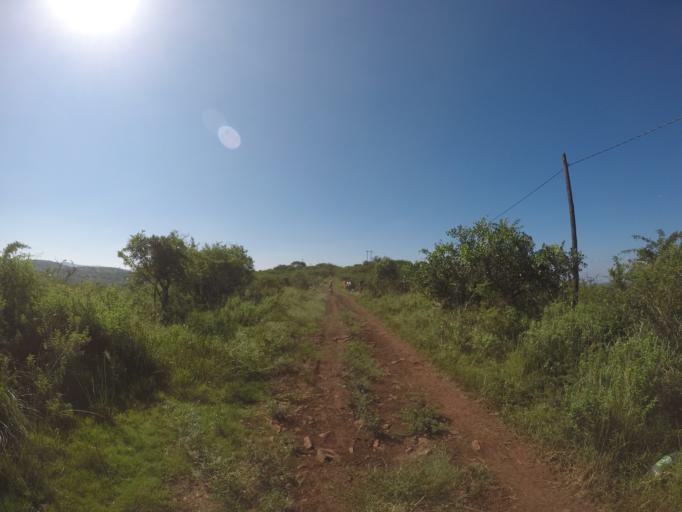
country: ZA
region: KwaZulu-Natal
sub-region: uThungulu District Municipality
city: Empangeni
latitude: -28.5722
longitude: 31.7104
